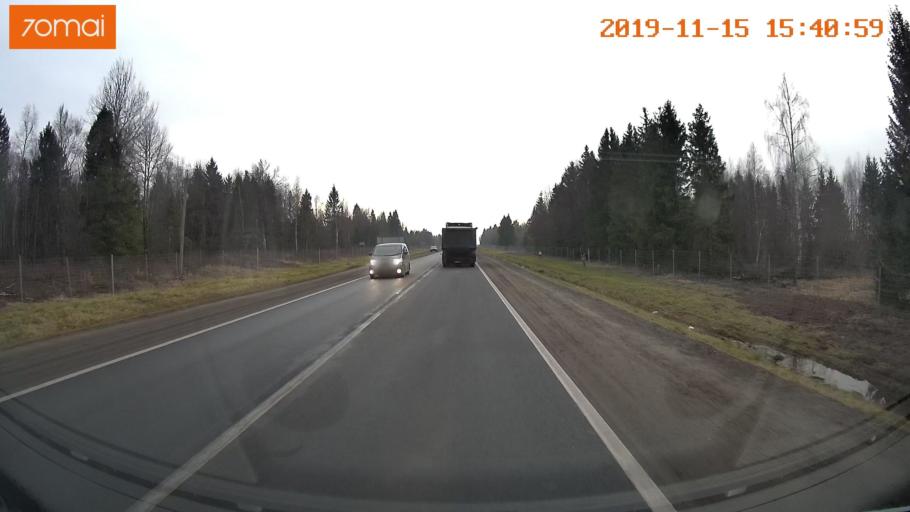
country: RU
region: Jaroslavl
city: Danilov
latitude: 58.0058
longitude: 40.0520
